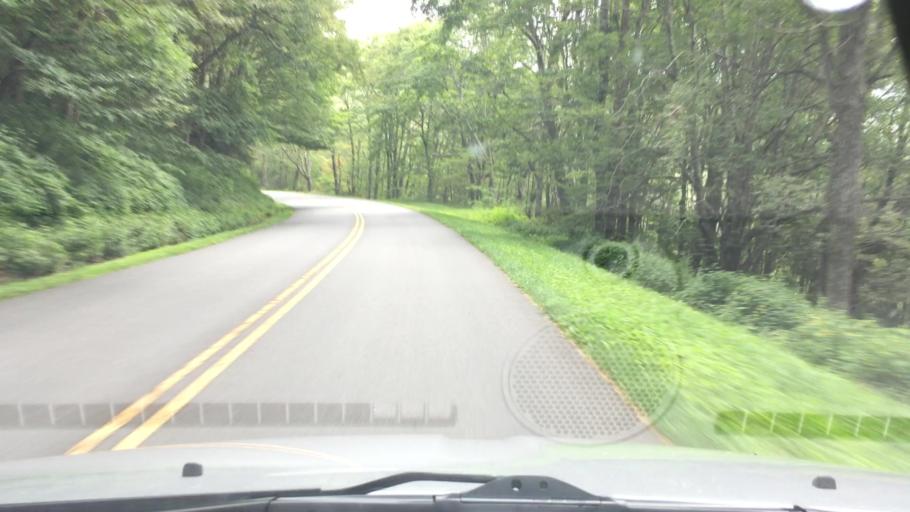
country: US
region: North Carolina
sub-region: Buncombe County
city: Swannanoa
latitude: 35.6972
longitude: -82.3965
